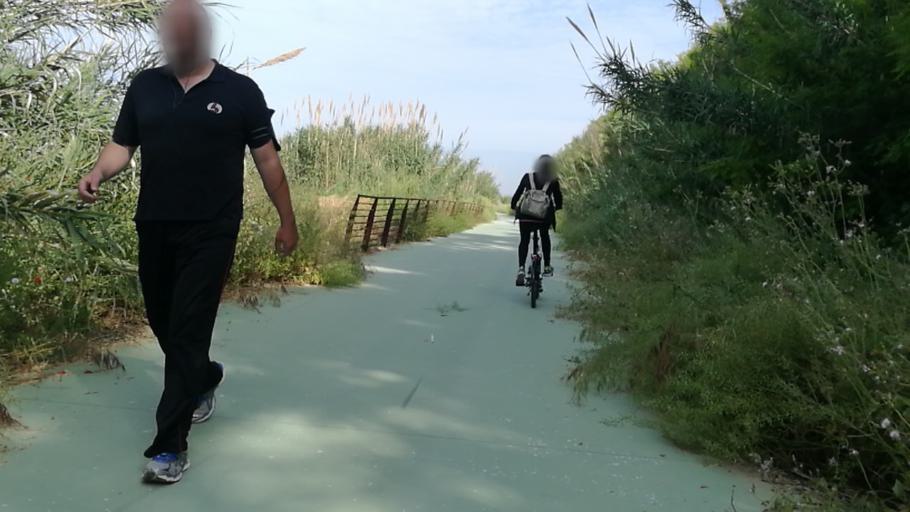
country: IT
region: Abruzzo
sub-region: Provincia di Chieti
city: Torino di Sangro
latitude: 42.2120
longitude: 14.5878
